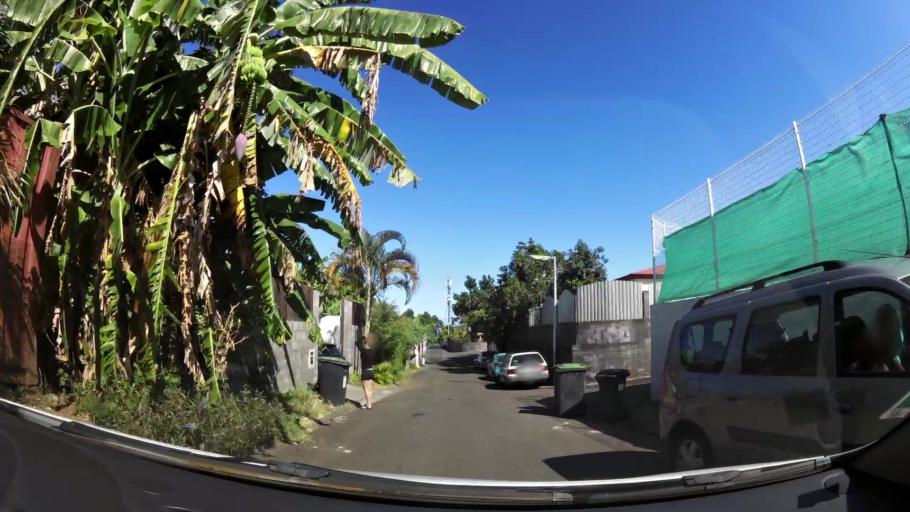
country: RE
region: Reunion
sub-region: Reunion
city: Le Tampon
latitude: -21.2771
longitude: 55.5075
